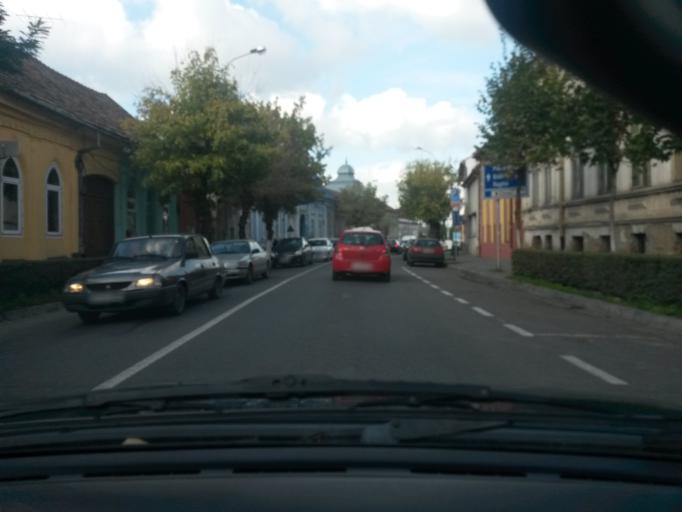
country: RO
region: Mures
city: Targu-Mures
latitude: 46.5500
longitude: 24.5648
